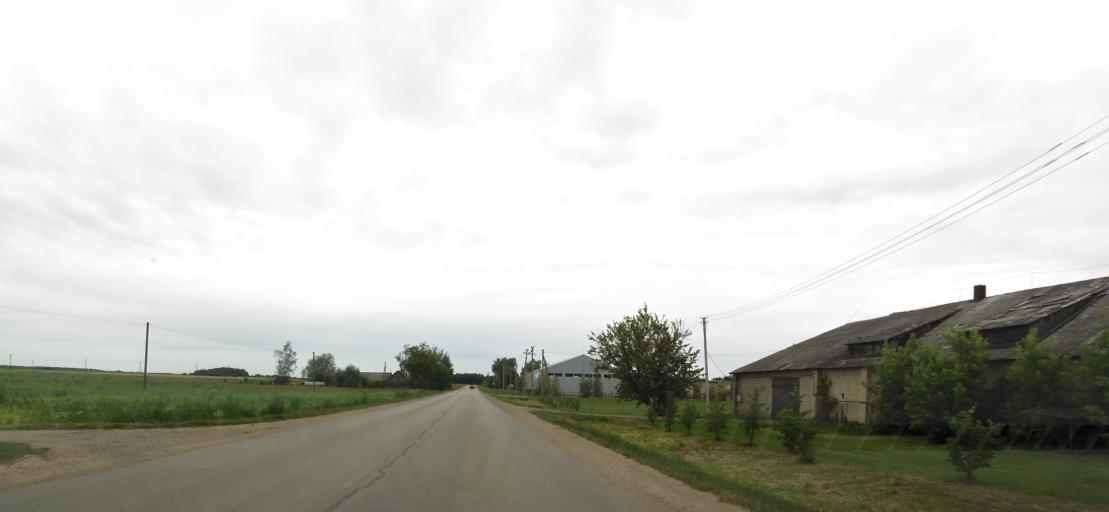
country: LT
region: Panevezys
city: Pasvalys
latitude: 56.0853
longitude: 24.5177
